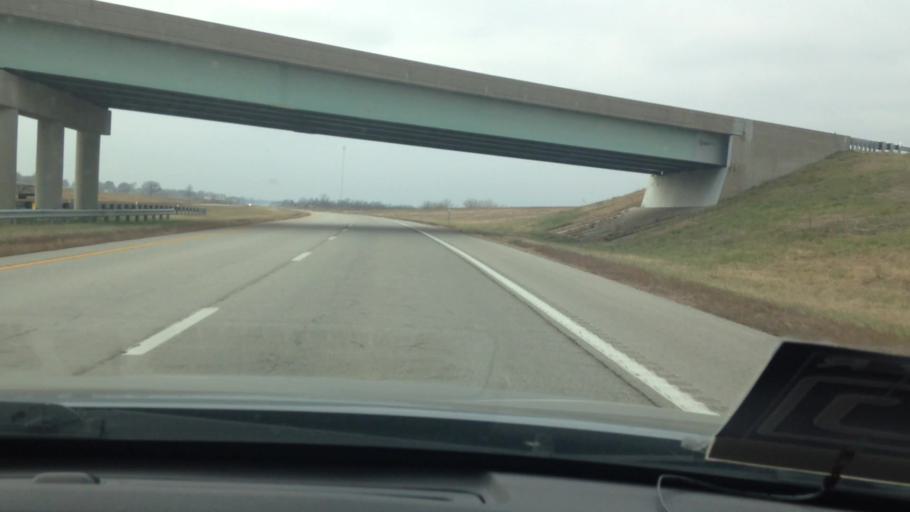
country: US
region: Missouri
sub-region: Cass County
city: Garden City
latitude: 38.5723
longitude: -94.1927
